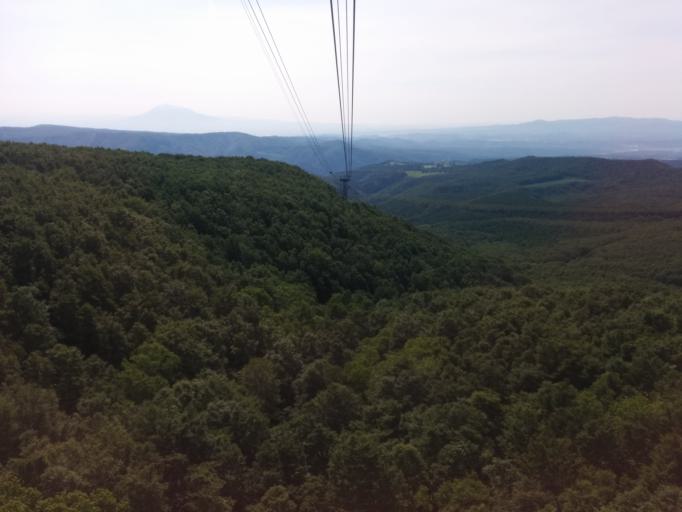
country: JP
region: Aomori
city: Aomori Shi
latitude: 40.6790
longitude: 140.8426
